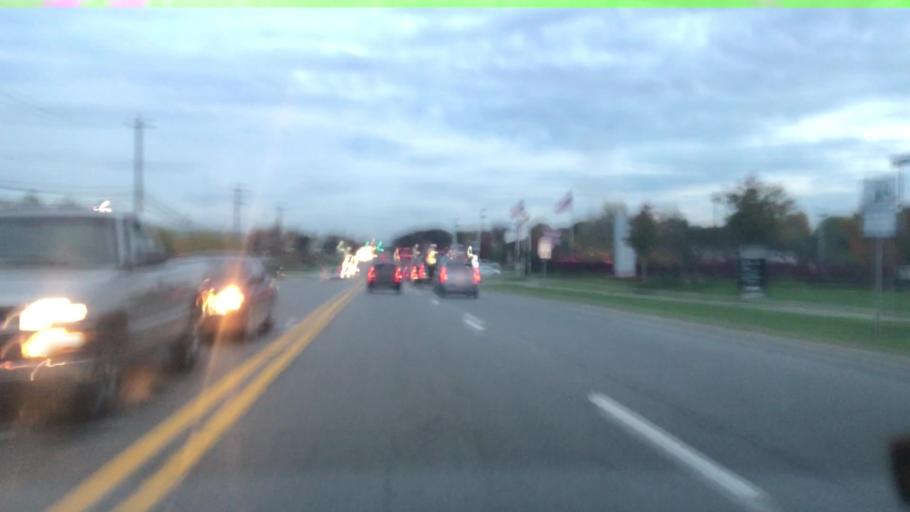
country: US
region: Michigan
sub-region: Oakland County
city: Bloomfield Hills
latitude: 42.6203
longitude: -83.2485
